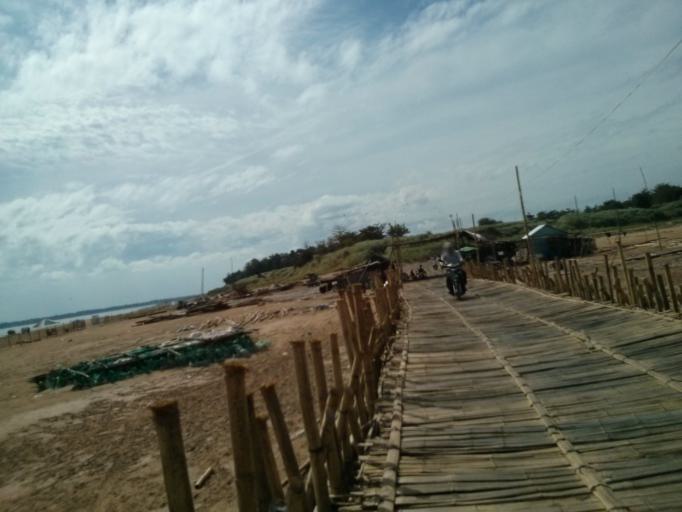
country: KH
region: Kampong Cham
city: Kampong Cham
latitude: 11.9709
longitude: 105.4628
